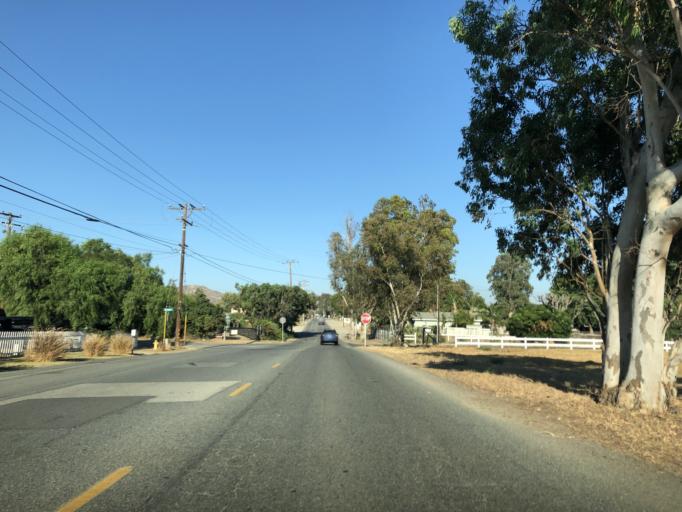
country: US
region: California
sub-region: Riverside County
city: Norco
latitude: 33.9095
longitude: -117.5767
